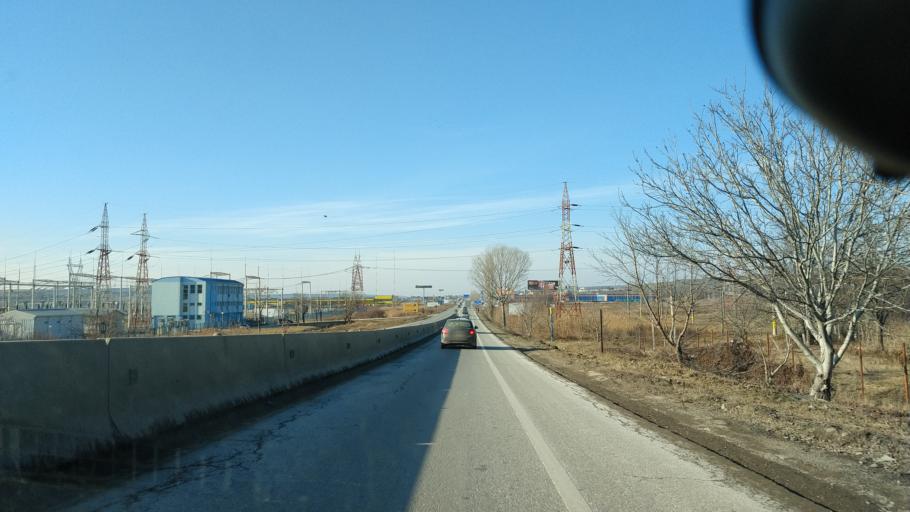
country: RO
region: Iasi
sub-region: Comuna Valea Lupului
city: Valea Lupului
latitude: 47.1785
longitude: 27.4842
